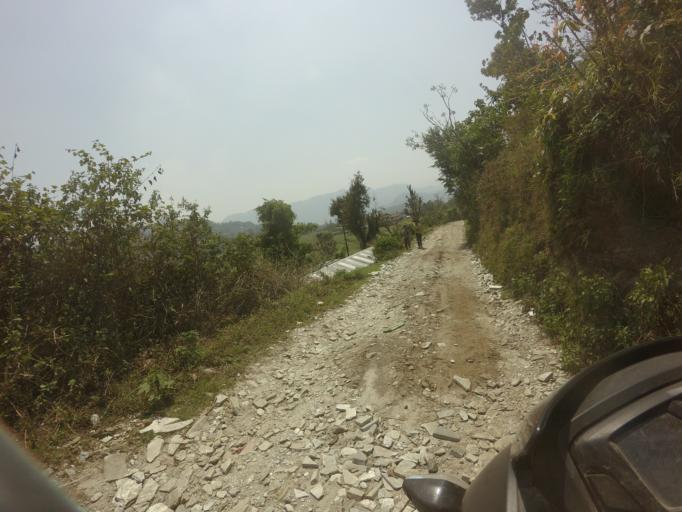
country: NP
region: Western Region
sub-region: Gandaki Zone
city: Pokhara
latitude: 28.3097
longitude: 83.9630
